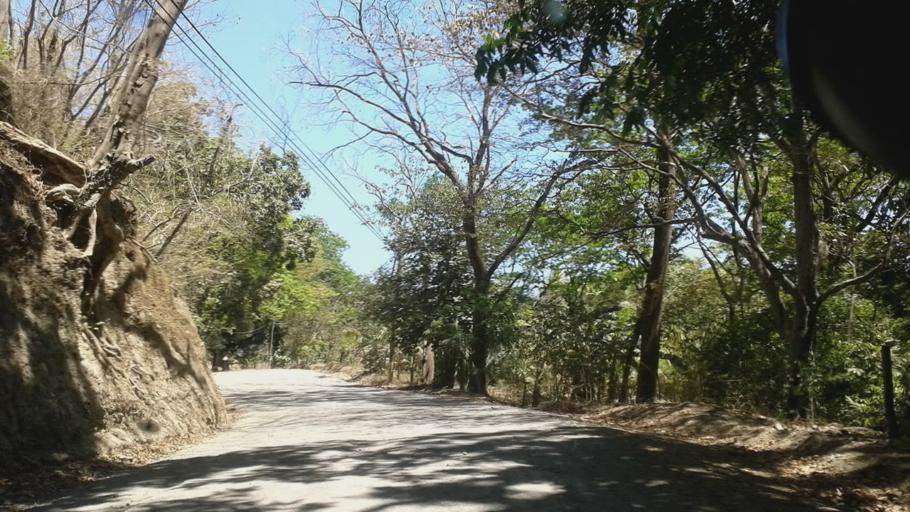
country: CR
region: Guanacaste
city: Samara
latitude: 9.9866
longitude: -85.6668
